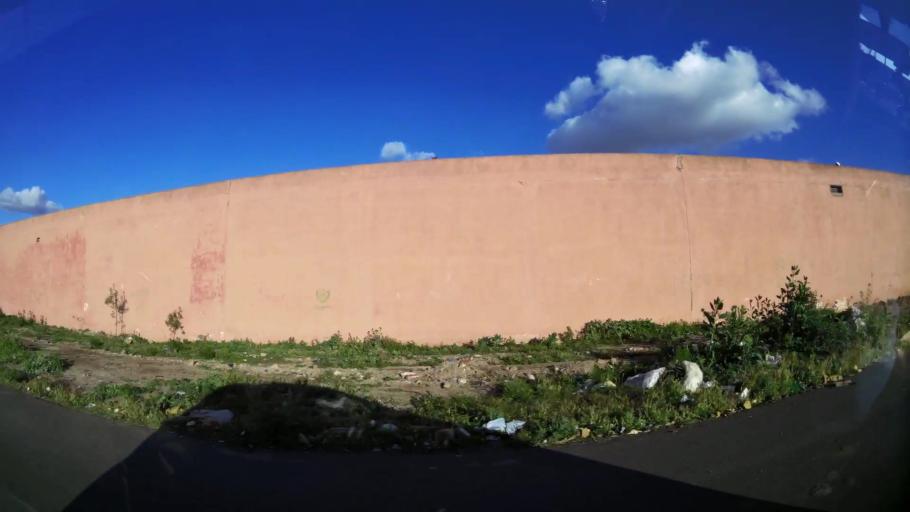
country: MA
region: Marrakech-Tensift-Al Haouz
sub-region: Kelaa-Des-Sraghna
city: Sidi Abdallah
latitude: 32.2388
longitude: -7.9650
